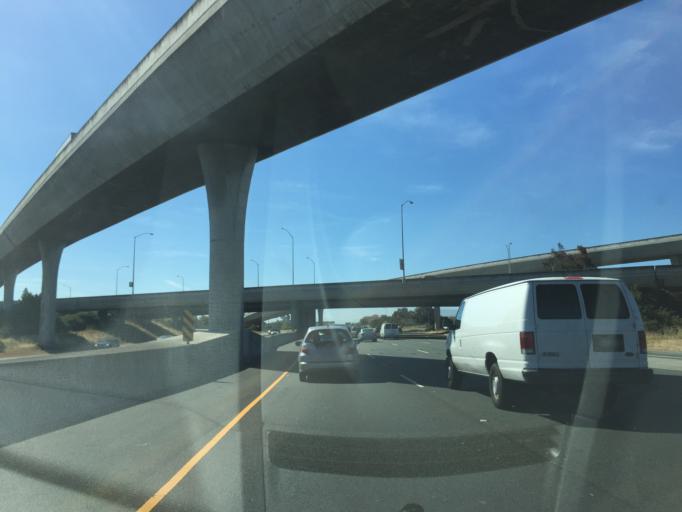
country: US
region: California
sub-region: San Mateo County
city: Foster City
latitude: 37.5542
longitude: -122.2971
